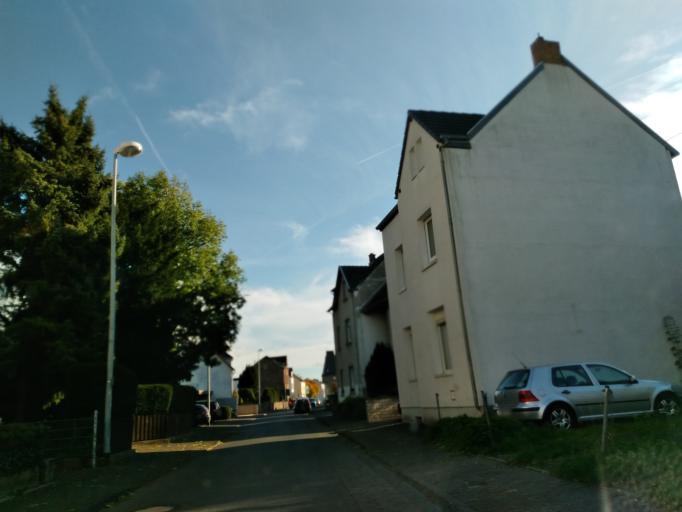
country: DE
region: Rheinland-Pfalz
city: Erpel
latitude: 50.5860
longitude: 7.2341
